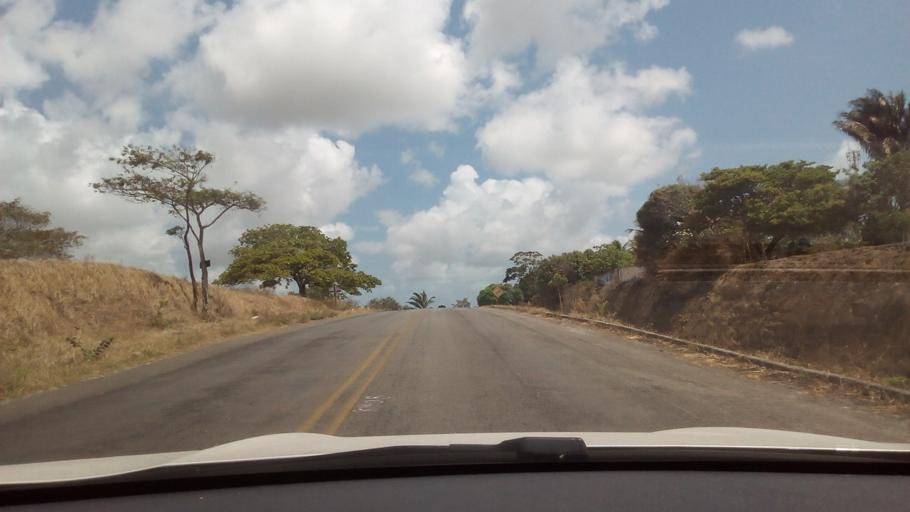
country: BR
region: Paraiba
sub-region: Conde
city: Conde
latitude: -7.2252
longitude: -34.8403
